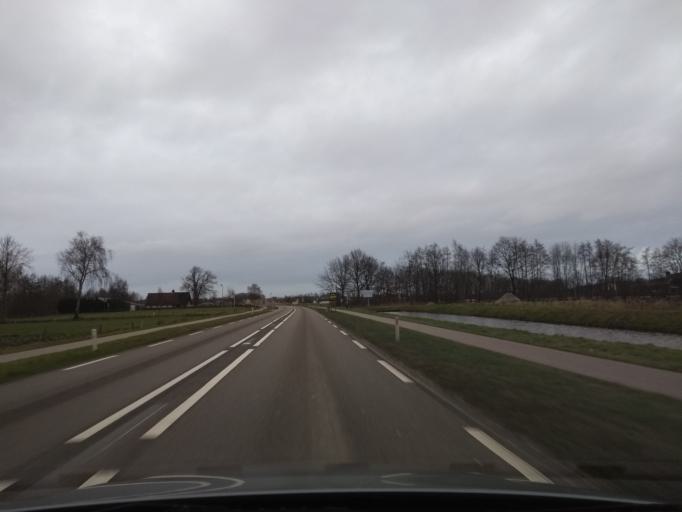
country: NL
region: Overijssel
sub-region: Gemeente Haaksbergen
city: Haaksbergen
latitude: 52.1769
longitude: 6.7400
